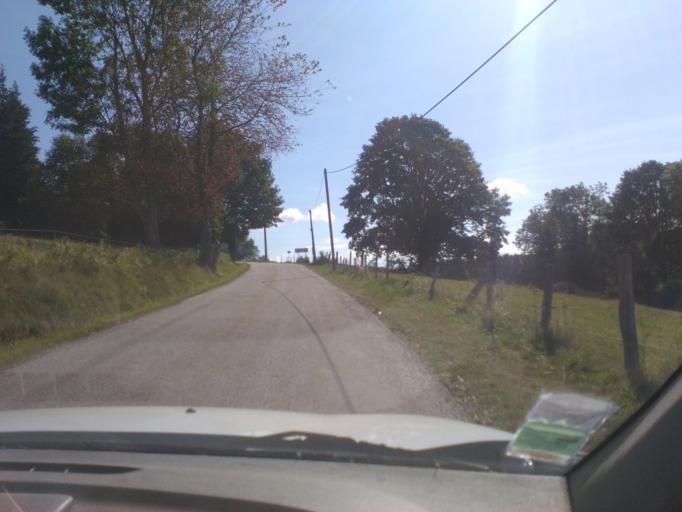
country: FR
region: Lorraine
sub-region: Departement des Vosges
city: Le Tholy
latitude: 48.0418
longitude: 6.7602
